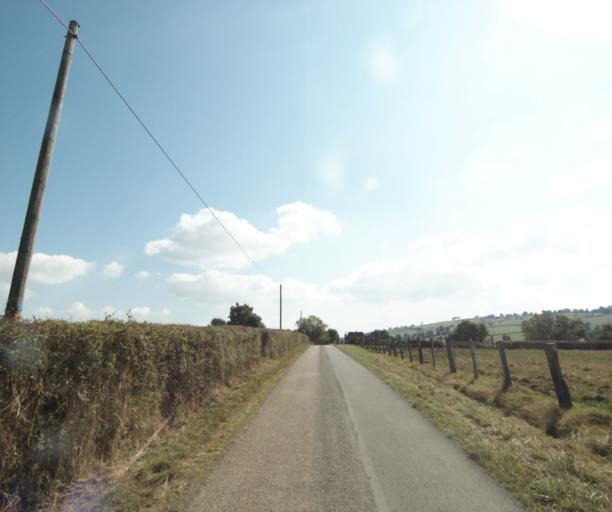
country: FR
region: Bourgogne
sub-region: Departement de Saone-et-Loire
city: Charolles
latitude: 46.3751
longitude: 4.2236
